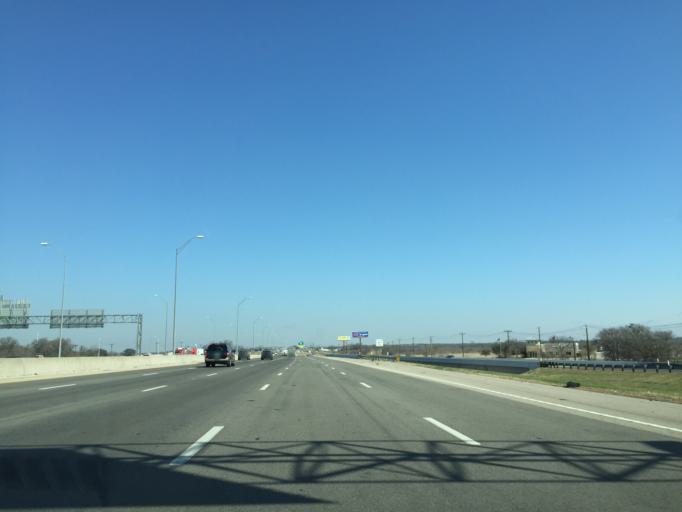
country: US
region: Texas
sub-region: Williamson County
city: Serenada
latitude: 30.7034
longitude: -97.6511
